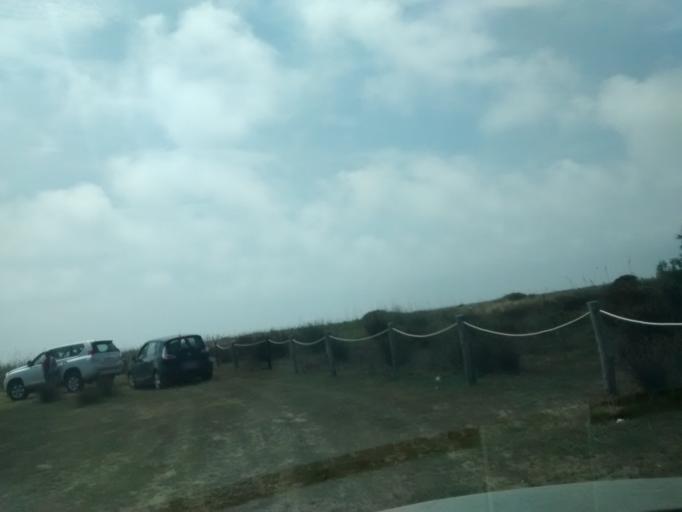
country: ES
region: Catalonia
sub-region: Provincia de Tarragona
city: Deltebre
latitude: 40.6845
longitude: 0.8529
